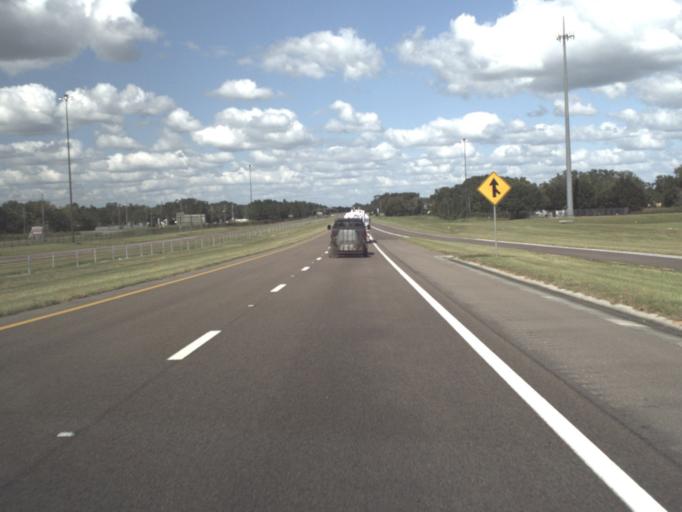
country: US
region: Florida
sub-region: Hernando County
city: Masaryktown
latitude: 28.4374
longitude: -82.4849
